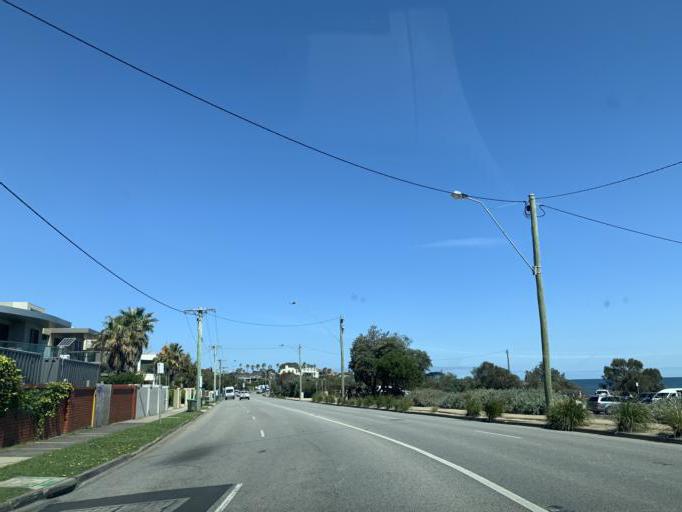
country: AU
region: Victoria
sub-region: Bayside
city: North Brighton
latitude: -37.9170
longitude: 144.9873
